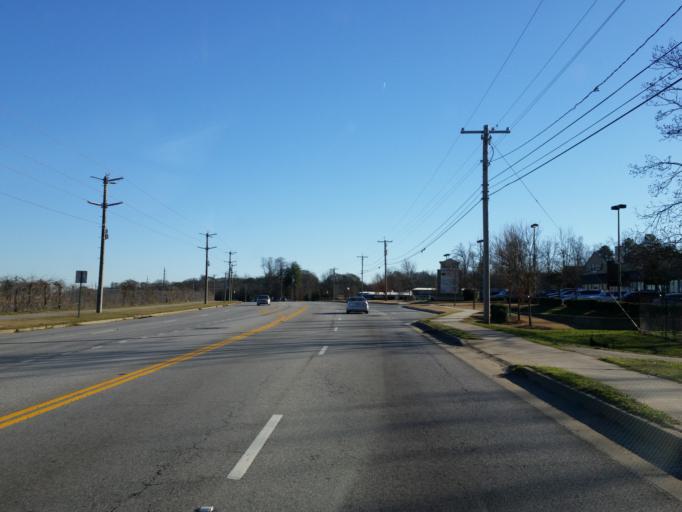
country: US
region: Georgia
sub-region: Cobb County
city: Fair Oaks
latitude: 33.9203
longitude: -84.5424
